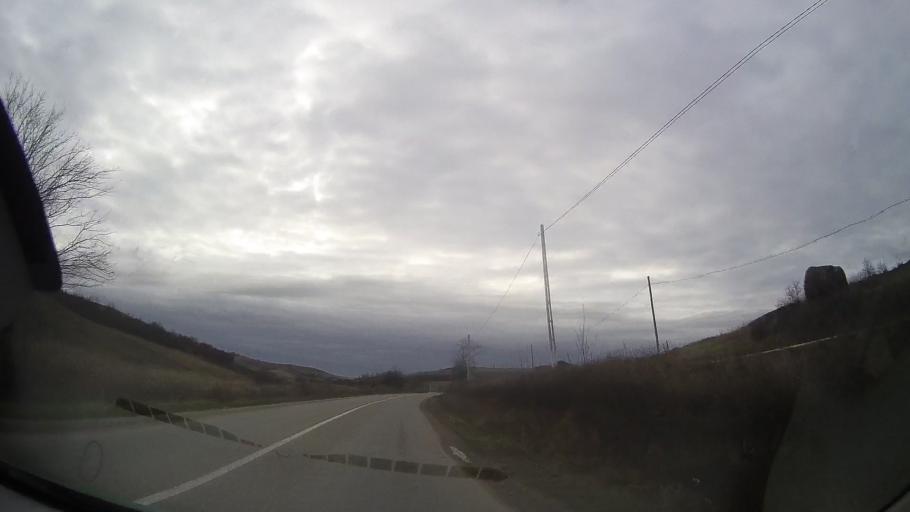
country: RO
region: Bistrita-Nasaud
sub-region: Comuna Budesti
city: Budesti
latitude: 46.8632
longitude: 24.2444
